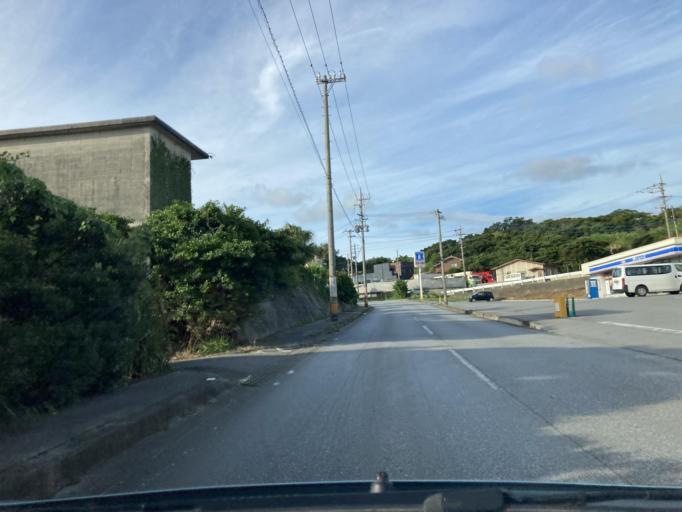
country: JP
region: Okinawa
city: Tomigusuku
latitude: 26.1453
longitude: 127.7452
